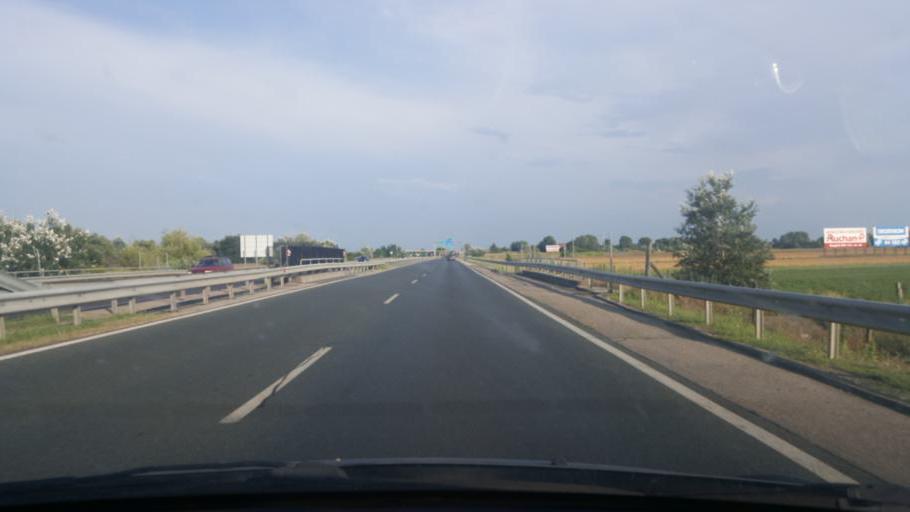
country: HU
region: Pest
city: Vecses
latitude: 47.4104
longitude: 19.2956
